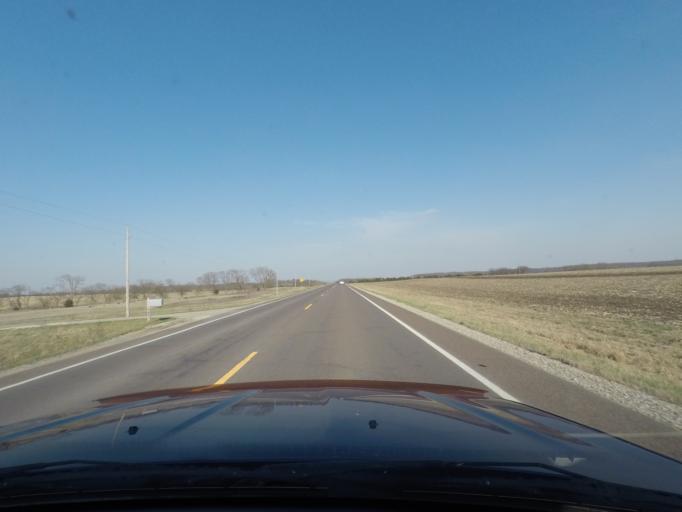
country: US
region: Kansas
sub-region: Douglas County
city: Lawrence
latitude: 39.0006
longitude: -95.3189
